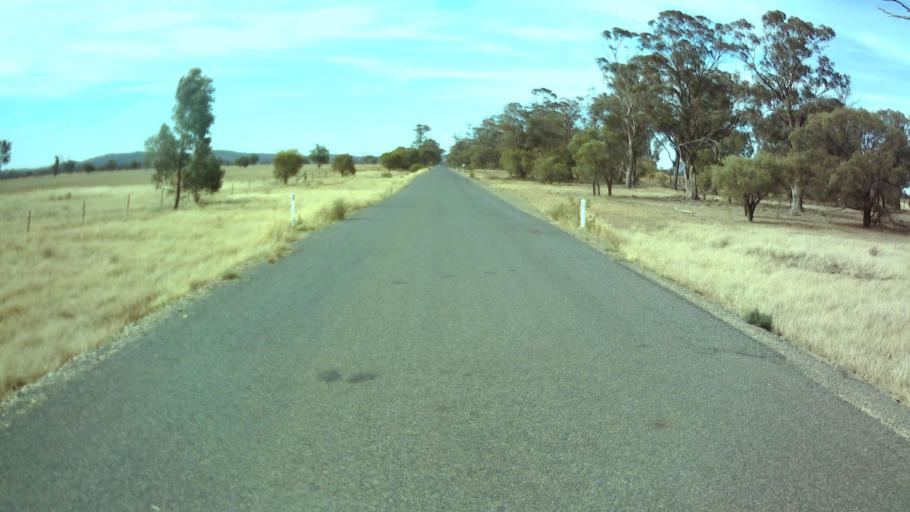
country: AU
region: New South Wales
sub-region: Weddin
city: Grenfell
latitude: -33.8739
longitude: 147.8575
